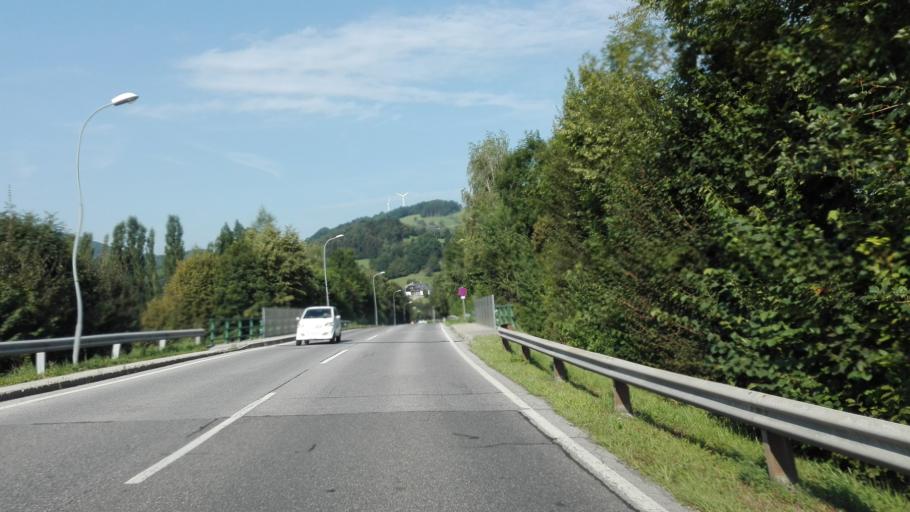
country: AT
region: Lower Austria
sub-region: Politischer Bezirk Lilienfeld
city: Traisen
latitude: 48.0501
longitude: 15.6177
